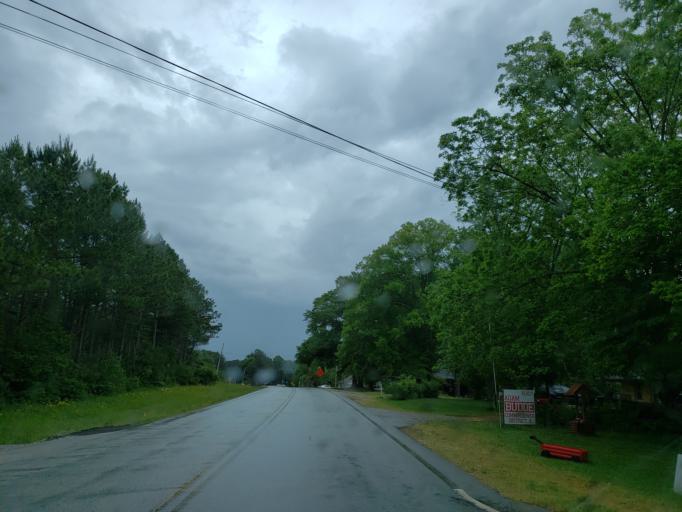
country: US
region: Georgia
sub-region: Haralson County
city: Buchanan
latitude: 33.7894
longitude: -85.1795
